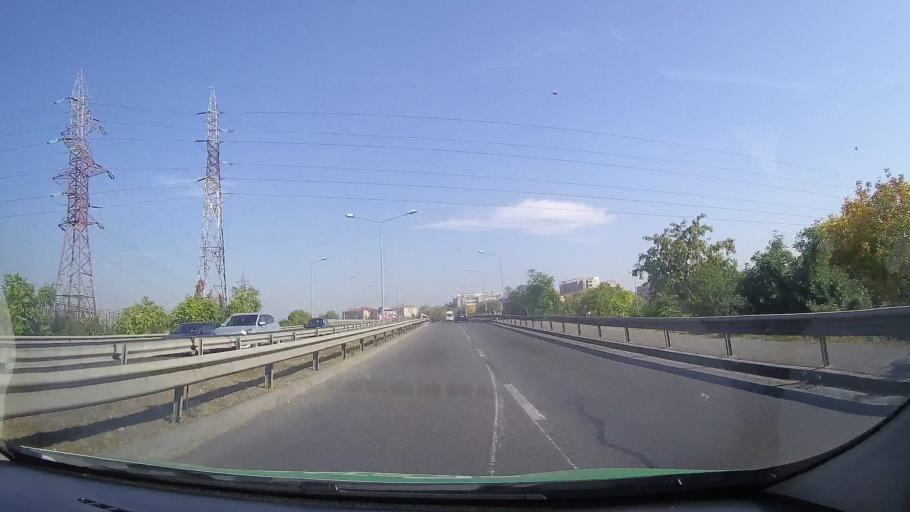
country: RO
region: Bihor
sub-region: Comuna Biharea
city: Oradea
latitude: 47.0708
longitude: 21.9039
